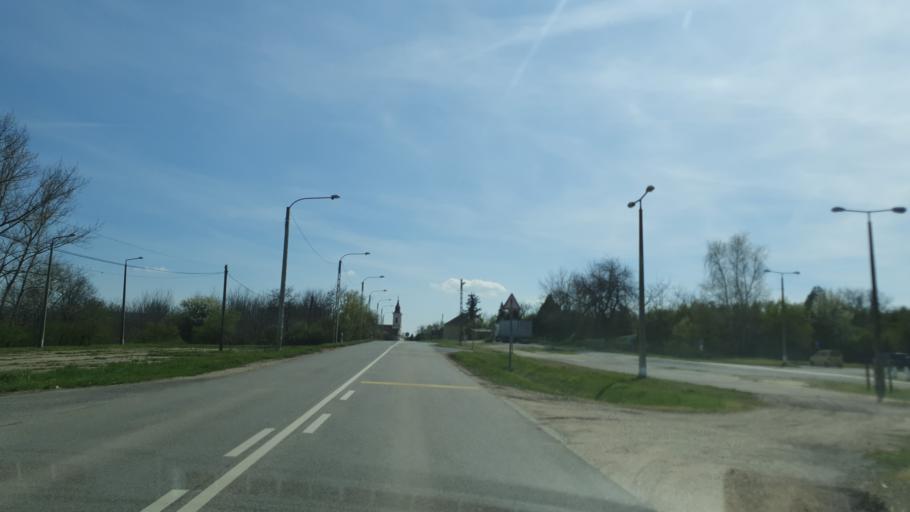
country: HU
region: Fejer
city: Pusztavam
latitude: 47.4404
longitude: 18.2341
